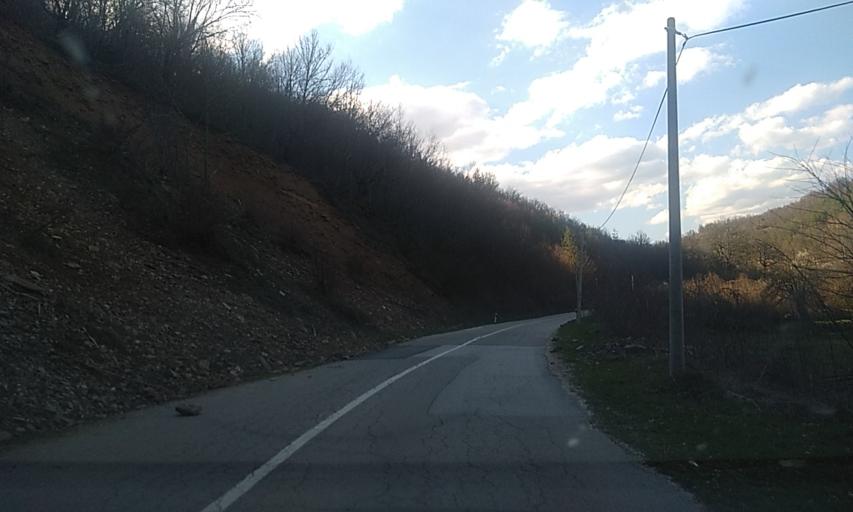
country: RS
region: Central Serbia
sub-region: Pcinjski Okrug
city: Bosilegrad
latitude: 42.4248
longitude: 22.5213
